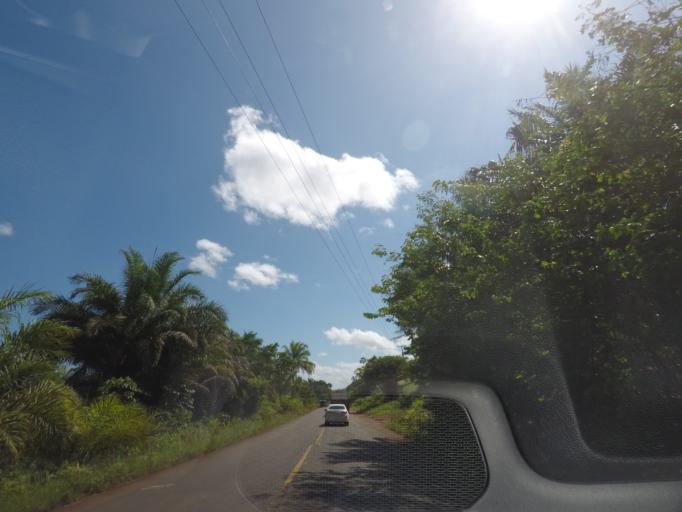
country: BR
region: Bahia
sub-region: Itubera
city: Itubera
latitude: -13.6691
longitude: -39.1214
